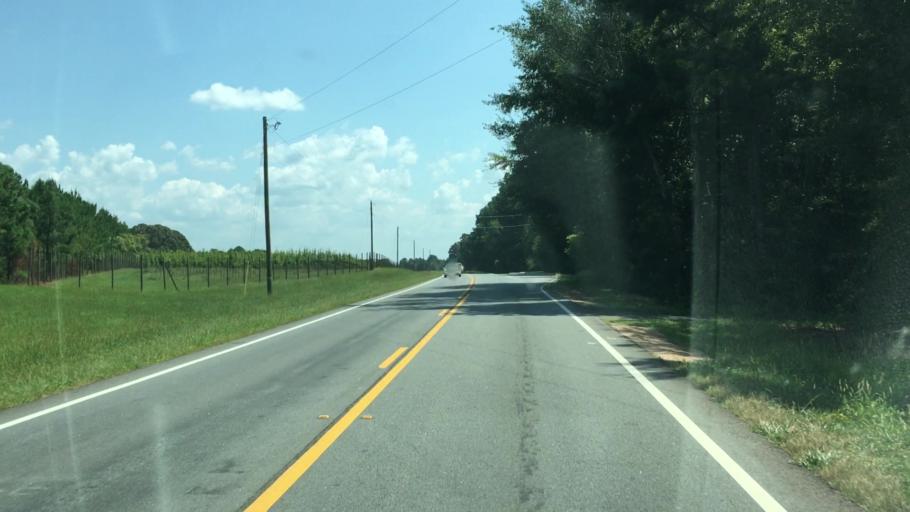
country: US
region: Georgia
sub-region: Oconee County
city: Watkinsville
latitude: 33.7505
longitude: -83.4345
